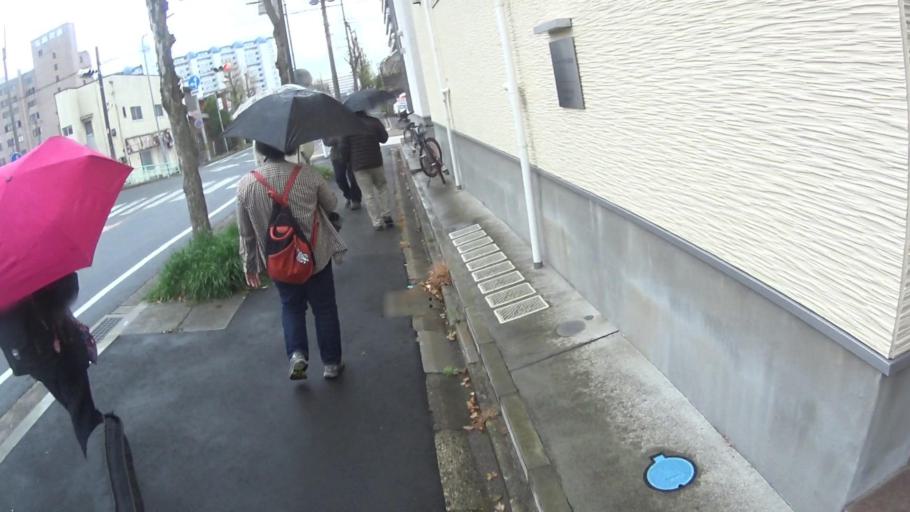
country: JP
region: Aichi
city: Nagoya-shi
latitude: 35.1159
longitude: 136.9102
